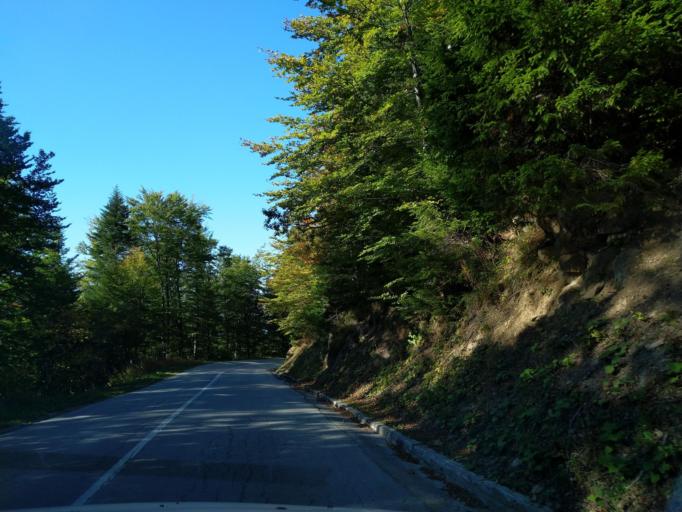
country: RS
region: Central Serbia
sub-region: Moravicki Okrug
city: Ivanjica
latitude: 43.4324
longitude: 20.2664
